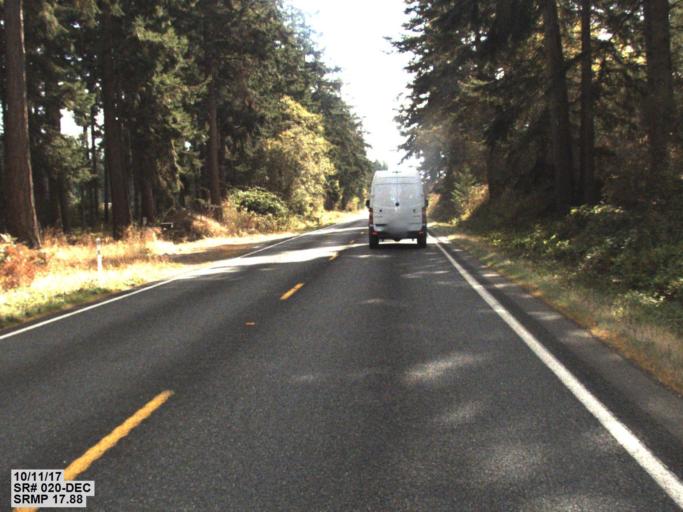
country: US
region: Washington
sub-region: Island County
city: Coupeville
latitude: 48.1881
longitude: -122.6266
